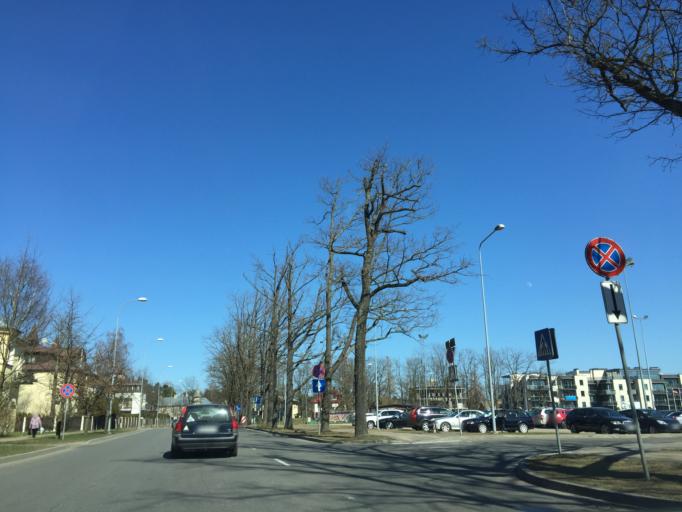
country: LV
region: Babite
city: Pinki
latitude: 56.9754
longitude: 23.8587
